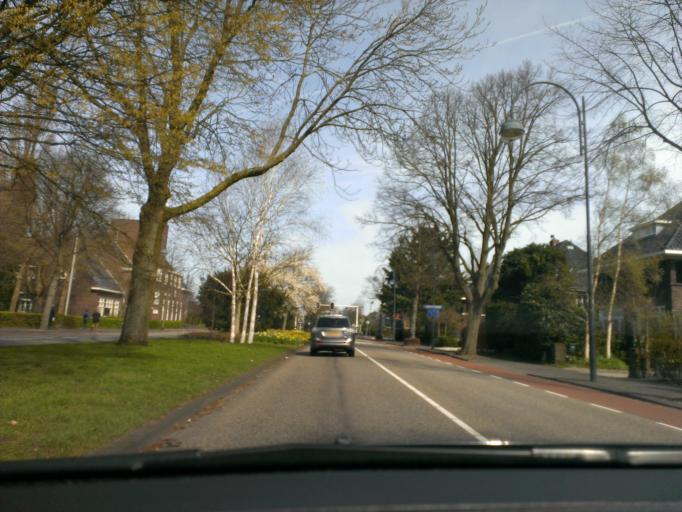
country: NL
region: North Holland
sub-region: Gemeente Heemstede
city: Heemstede
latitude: 52.3517
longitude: 4.6246
